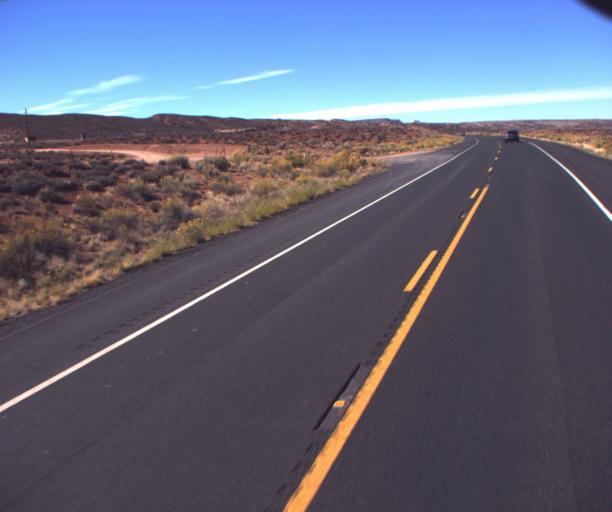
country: US
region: Arizona
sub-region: Coconino County
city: Tuba City
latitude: 36.3122
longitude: -111.4695
